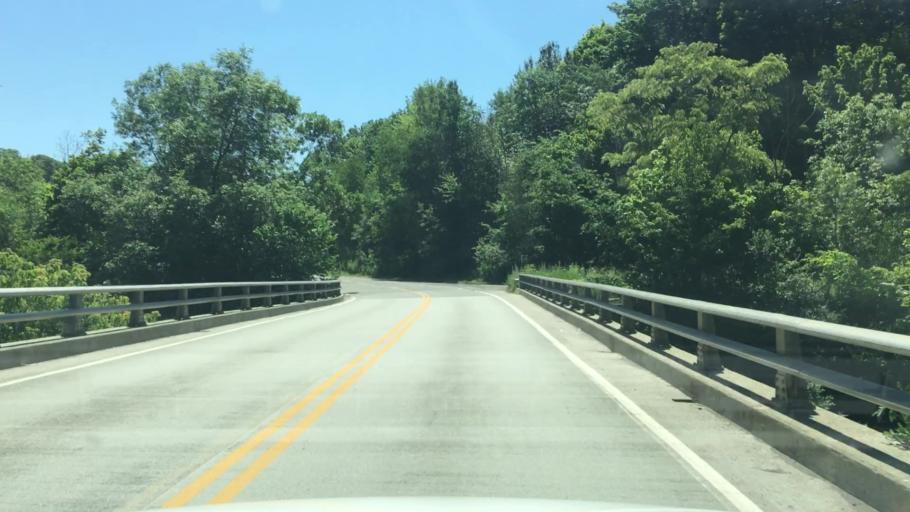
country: US
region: Maine
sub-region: Penobscot County
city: Bangor
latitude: 44.8134
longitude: -68.7837
